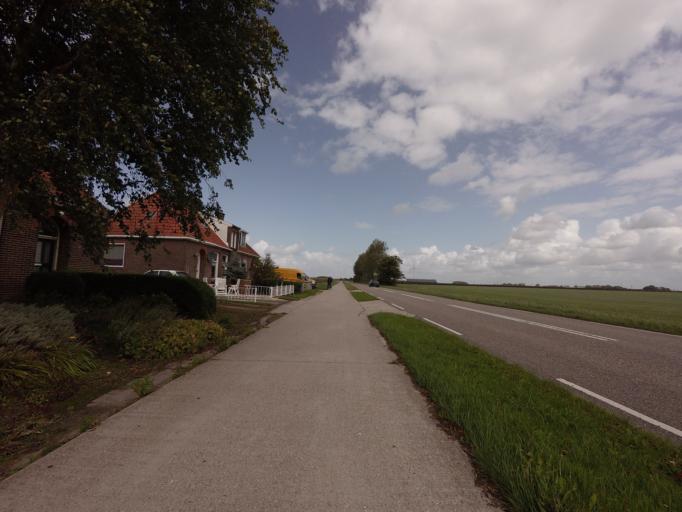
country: NL
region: Friesland
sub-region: Gemeente Harlingen
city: Harlingen
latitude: 53.1342
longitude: 5.4708
